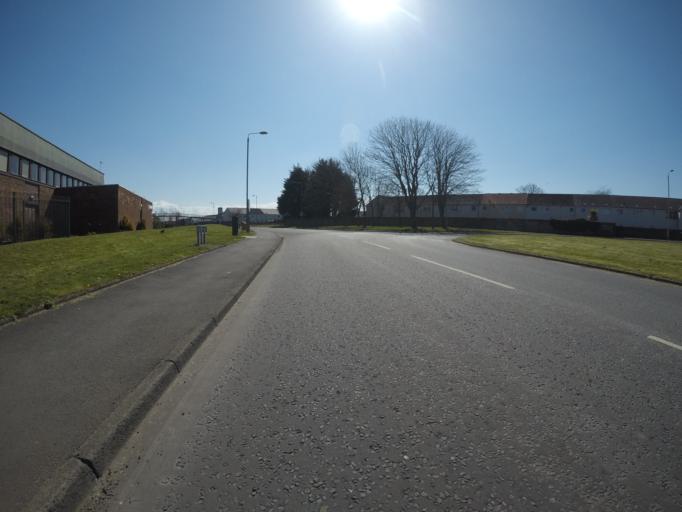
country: GB
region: Scotland
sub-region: North Ayrshire
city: Irvine
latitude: 55.6300
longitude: -4.6675
